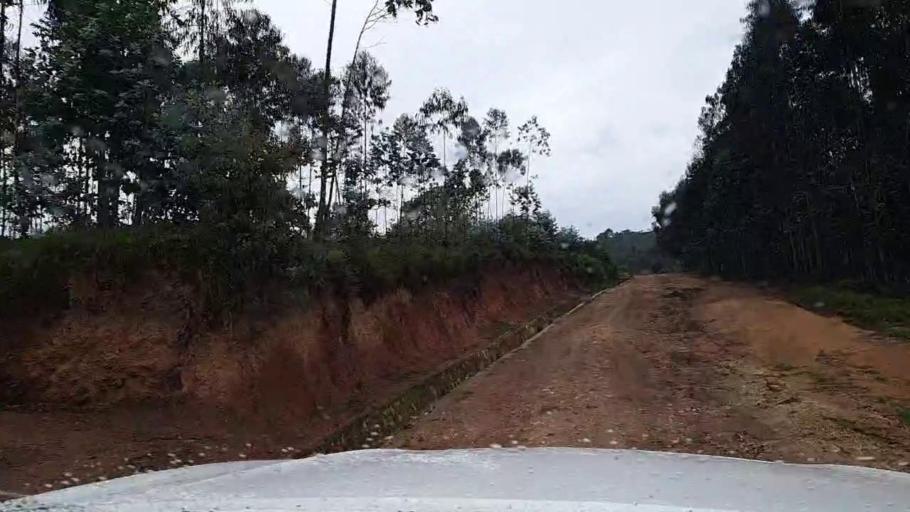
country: RW
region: Southern Province
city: Nzega
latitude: -2.4677
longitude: 29.5027
